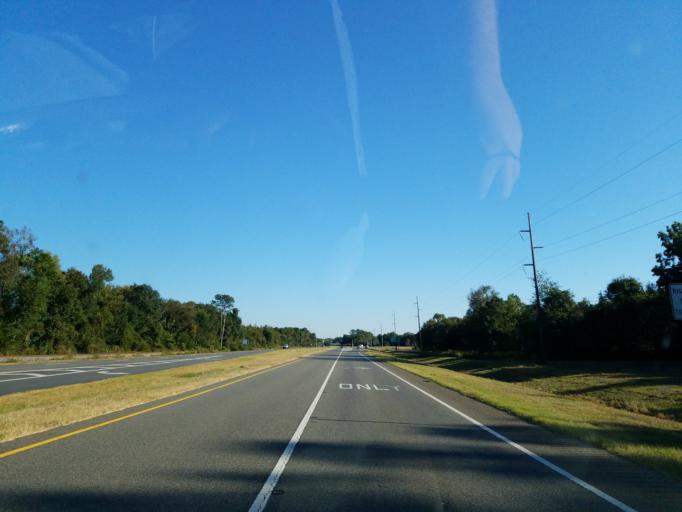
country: US
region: Georgia
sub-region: Lee County
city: Leesburg
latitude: 31.7441
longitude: -84.1780
